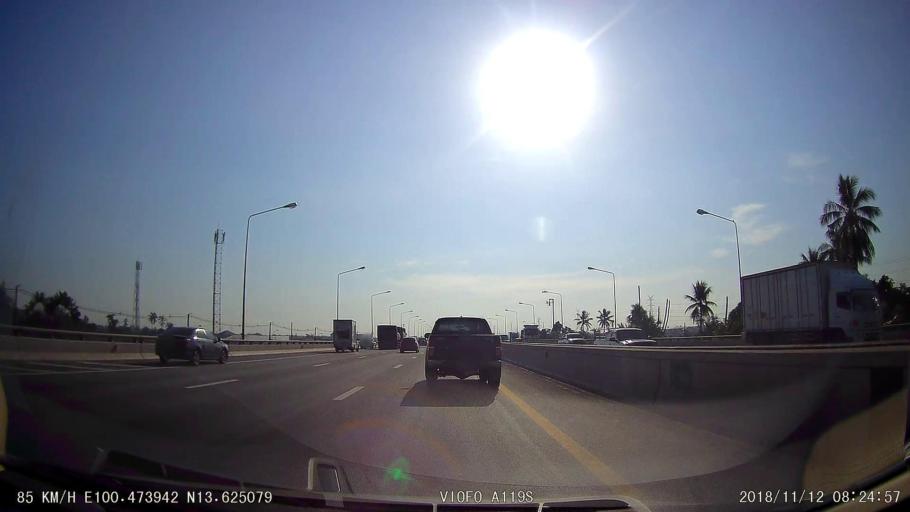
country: TH
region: Bangkok
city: Thung Khru
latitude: 13.6250
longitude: 100.4741
